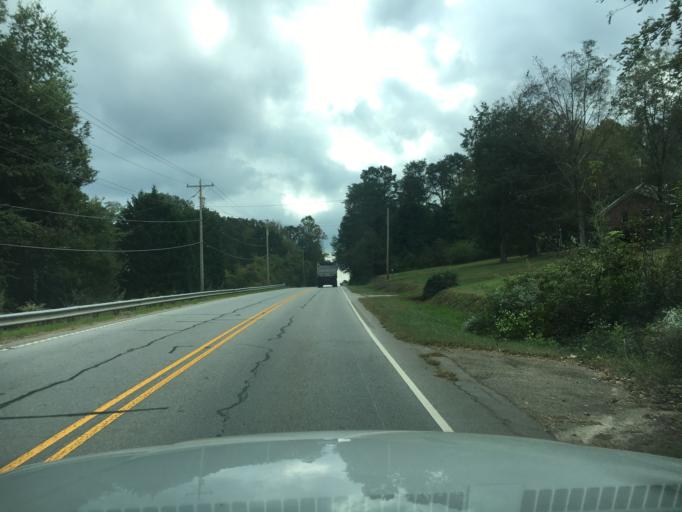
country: US
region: South Carolina
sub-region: Greenville County
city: Greer
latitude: 34.9762
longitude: -82.2422
